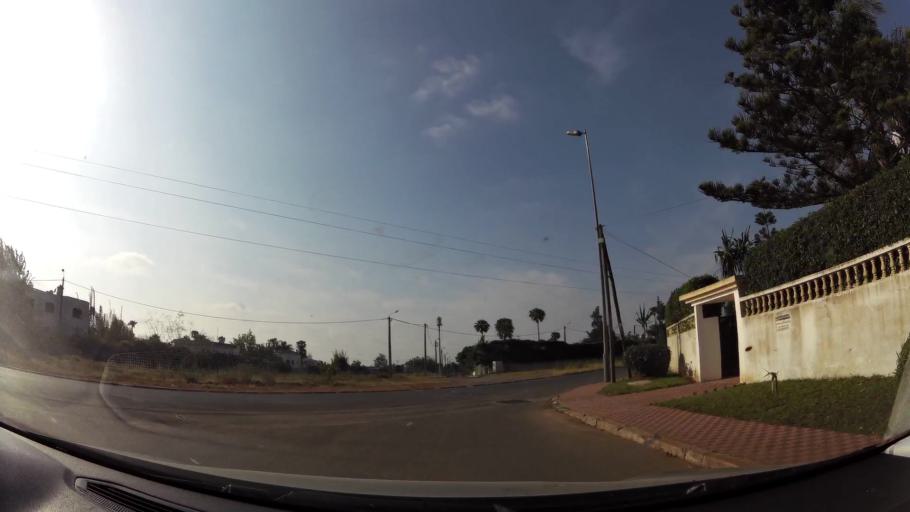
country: MA
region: Rabat-Sale-Zemmour-Zaer
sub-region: Rabat
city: Rabat
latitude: 33.9375
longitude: -6.8088
